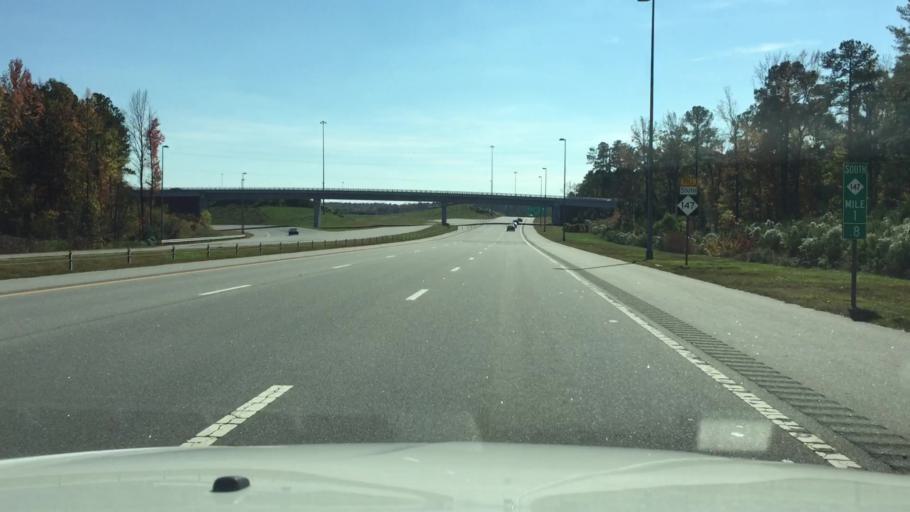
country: US
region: North Carolina
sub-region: Wake County
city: Morrisville
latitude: 35.8611
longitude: -78.8641
